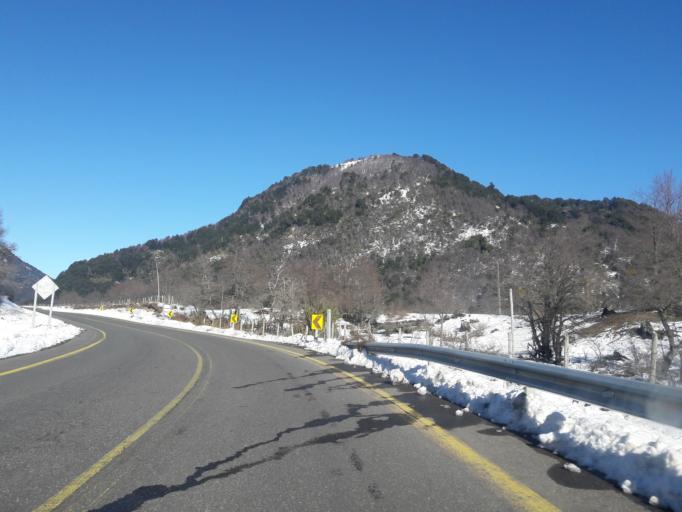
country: CL
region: Araucania
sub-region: Provincia de Cautin
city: Vilcun
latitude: -38.4813
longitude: -71.5364
